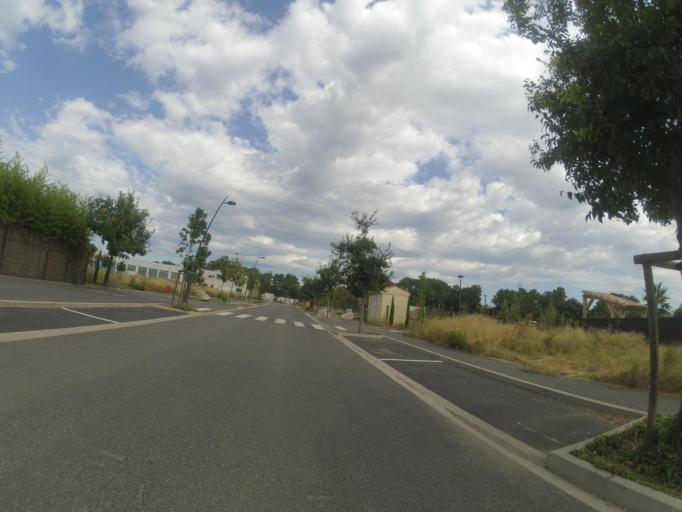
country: FR
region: Languedoc-Roussillon
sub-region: Departement des Pyrenees-Orientales
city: Toulouges
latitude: 42.6752
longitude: 2.8268
